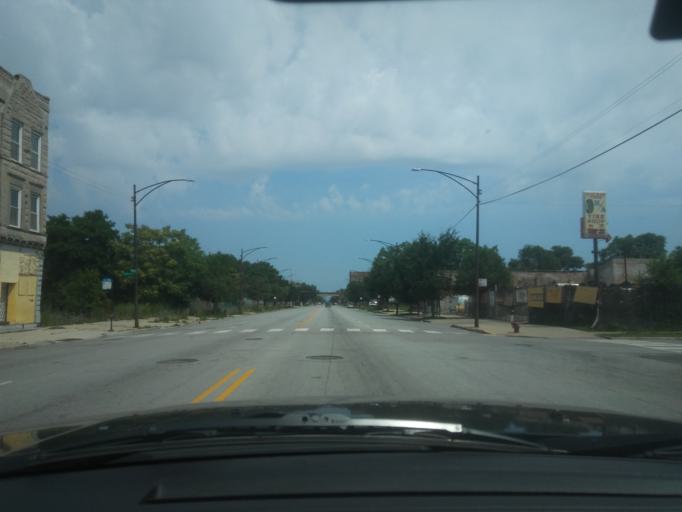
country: US
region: Illinois
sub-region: Cook County
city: Chicago
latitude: 41.7835
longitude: -87.6254
